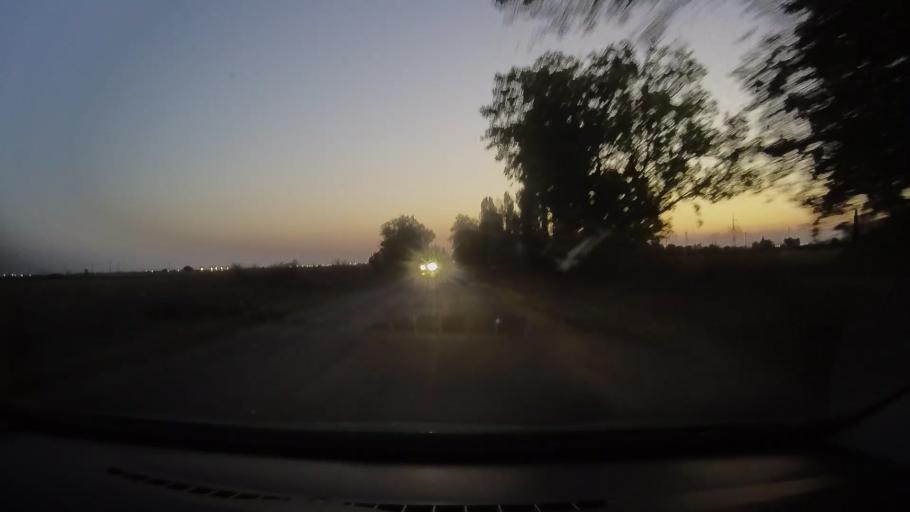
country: RO
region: Arad
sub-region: Comuna Vladimirescu
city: Vladimirescu
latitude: 46.1890
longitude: 21.3917
